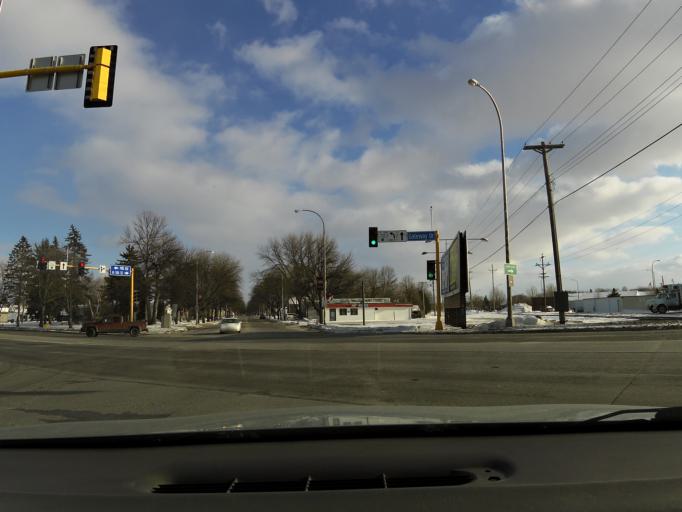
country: US
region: North Dakota
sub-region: Grand Forks County
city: Grand Forks
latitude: 47.9333
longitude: -97.0494
